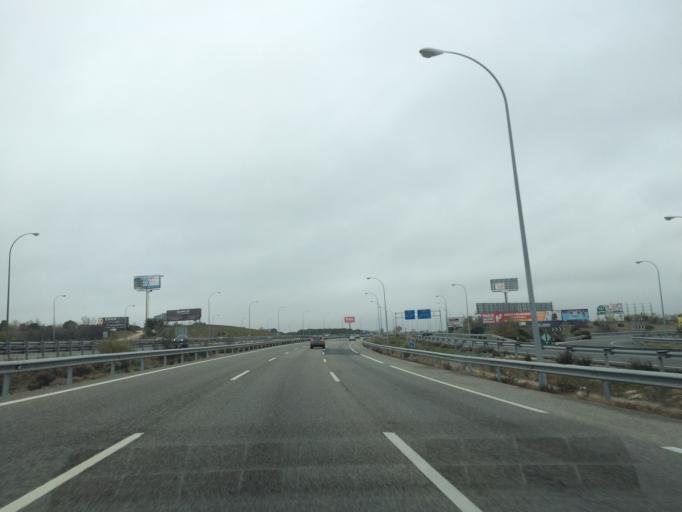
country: ES
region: Madrid
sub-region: Provincia de Madrid
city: Pozuelo de Alarcon
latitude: 40.4251
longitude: -3.8348
